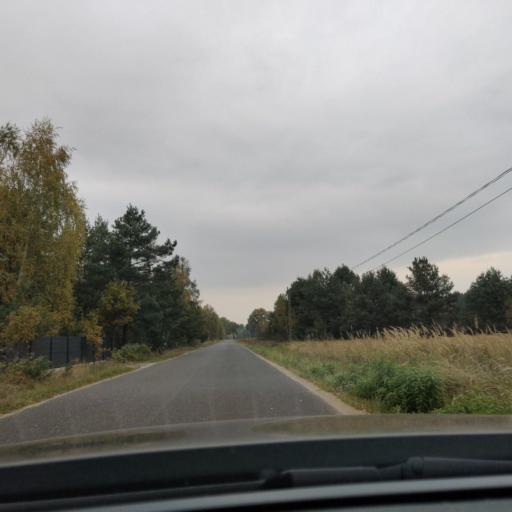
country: PL
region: Masovian Voivodeship
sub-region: Powiat sochaczewski
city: Brochow
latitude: 52.3078
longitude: 20.3228
